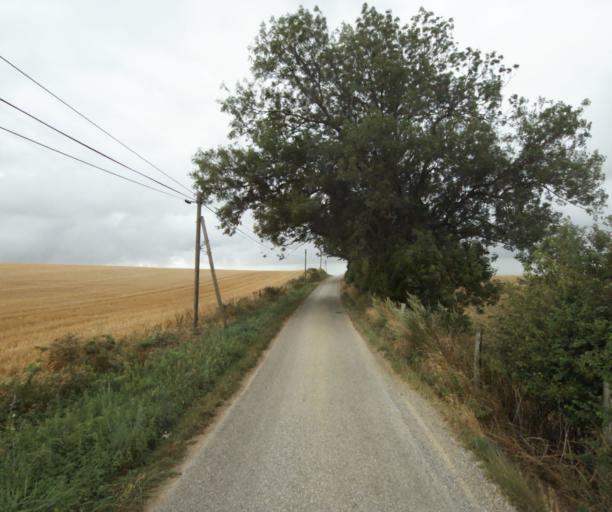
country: FR
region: Midi-Pyrenees
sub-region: Departement du Tarn
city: Soreze
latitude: 43.3944
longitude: 2.0515
